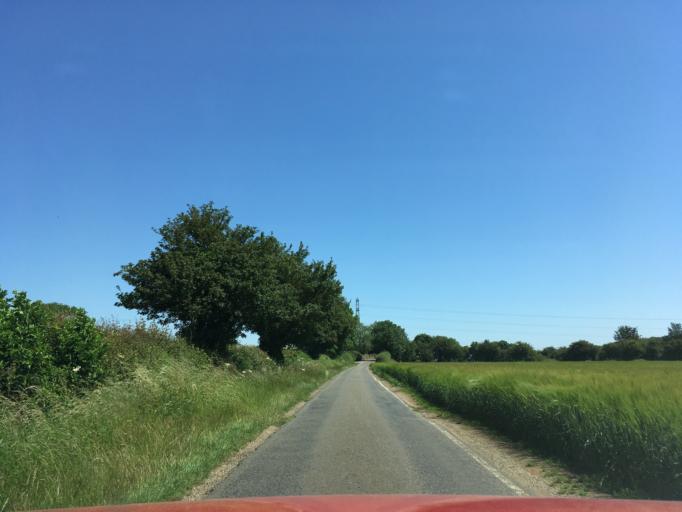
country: GB
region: England
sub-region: Northamptonshire
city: Brackley
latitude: 51.9985
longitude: -1.1036
